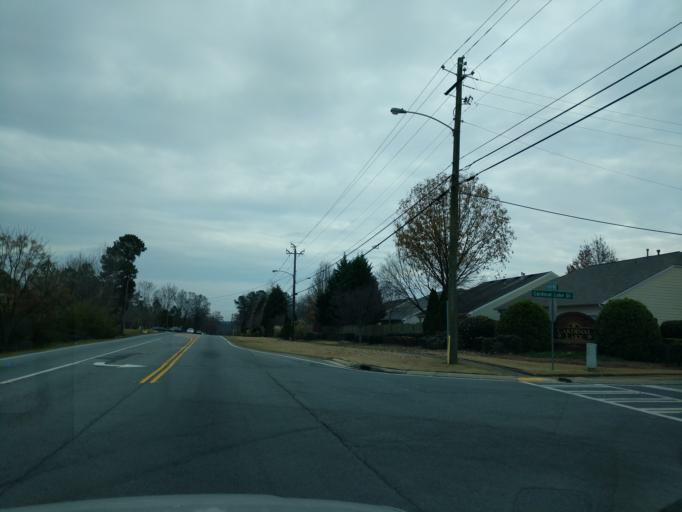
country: US
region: Georgia
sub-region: Gwinnett County
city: Duluth
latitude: 33.9815
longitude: -84.1178
